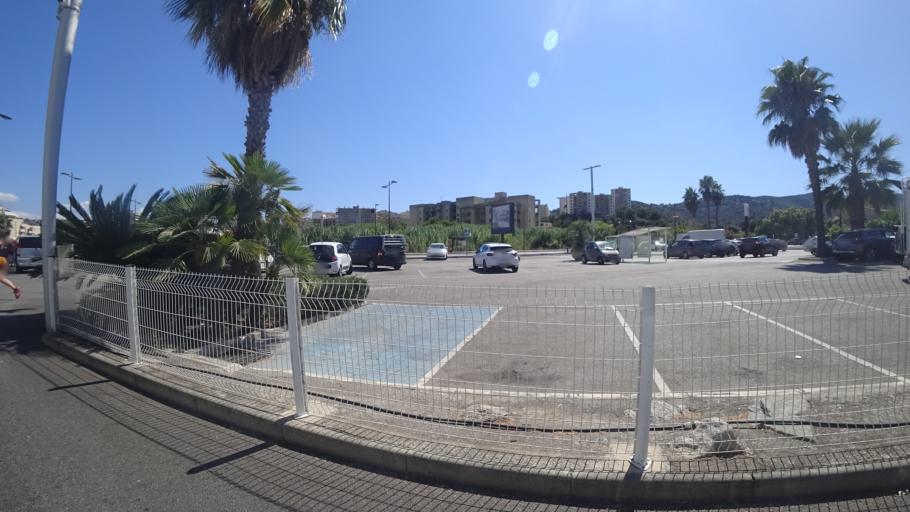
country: FR
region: Corsica
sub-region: Departement de la Corse-du-Sud
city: Ajaccio
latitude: 41.9374
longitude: 8.7367
